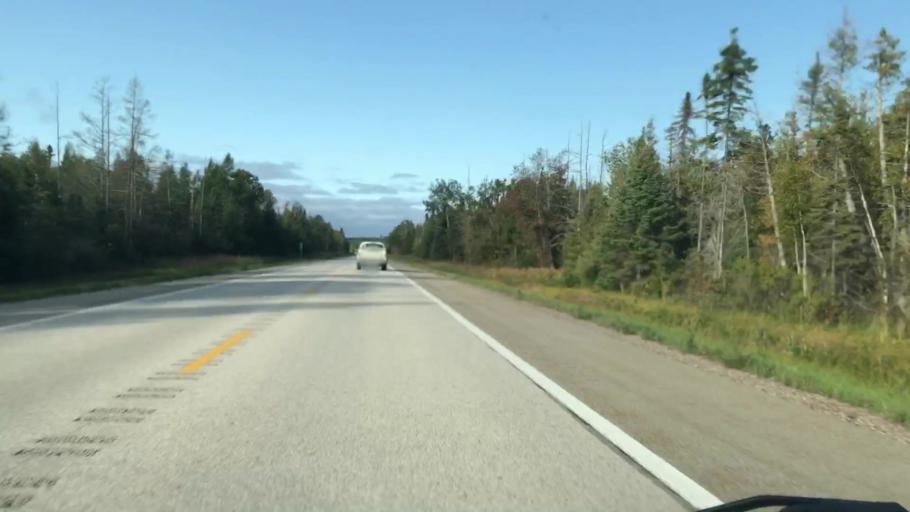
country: US
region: Michigan
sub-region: Luce County
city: Newberry
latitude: 46.3212
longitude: -85.1833
